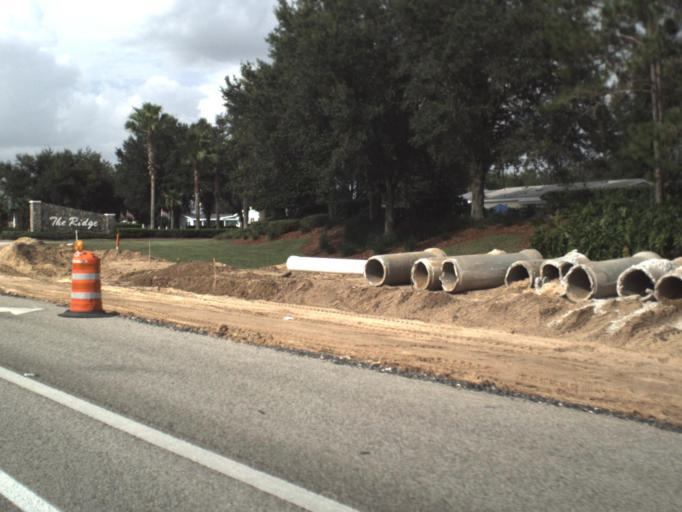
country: US
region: Florida
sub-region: Lake County
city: Four Corners
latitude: 28.2987
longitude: -81.6656
